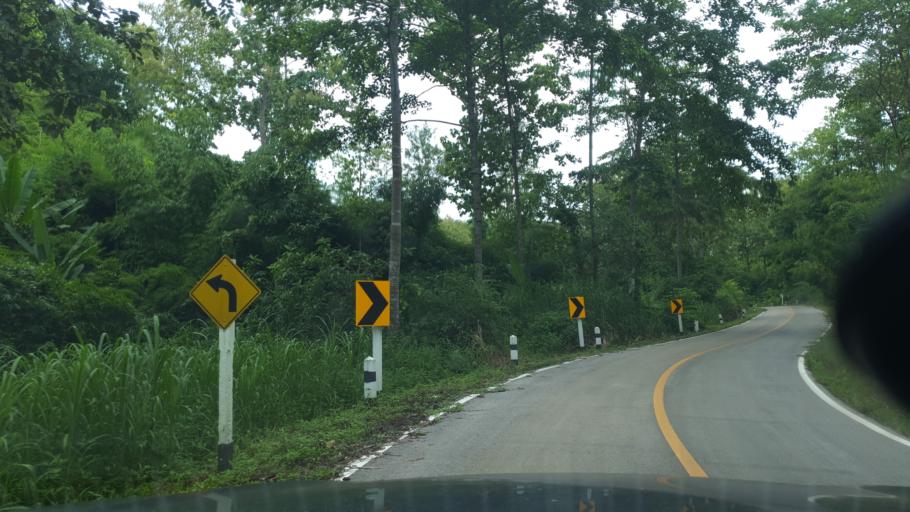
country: TH
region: Lampang
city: Hang Chat
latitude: 18.3779
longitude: 99.2598
